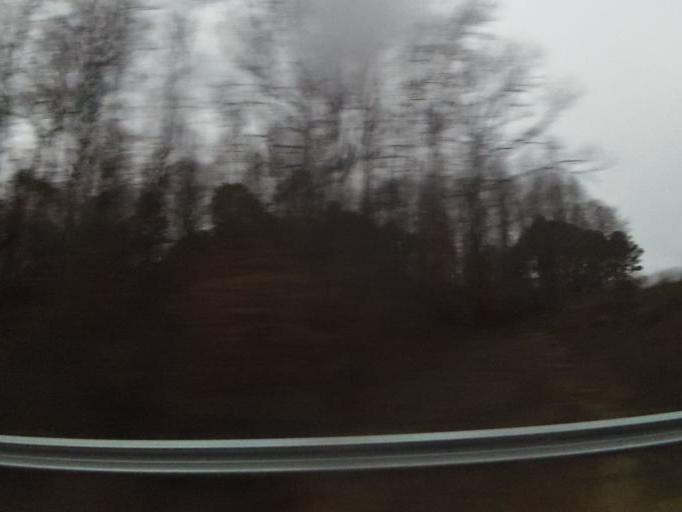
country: US
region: Alabama
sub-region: Cullman County
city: Cullman
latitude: 34.2203
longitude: -86.8760
